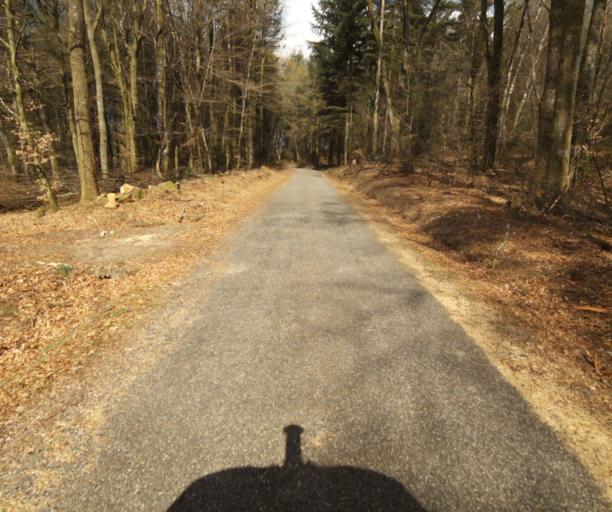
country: FR
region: Limousin
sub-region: Departement de la Correze
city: Argentat
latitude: 45.2358
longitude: 1.9414
